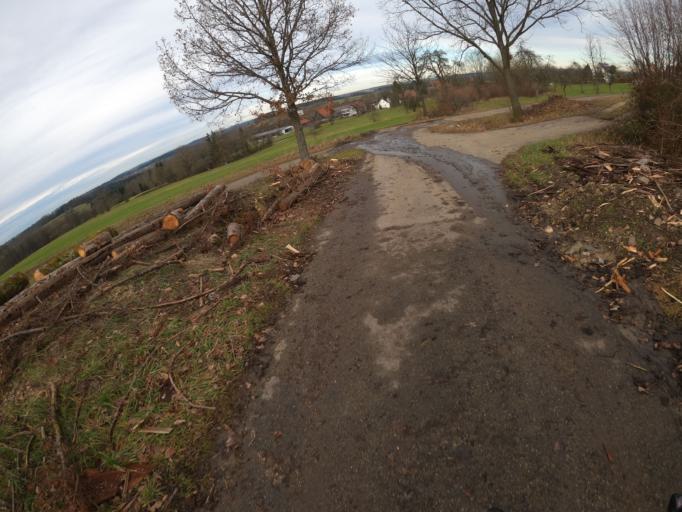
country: DE
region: Baden-Wuerttemberg
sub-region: Regierungsbezirk Stuttgart
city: Ottenbach
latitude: 48.7598
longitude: 9.7576
